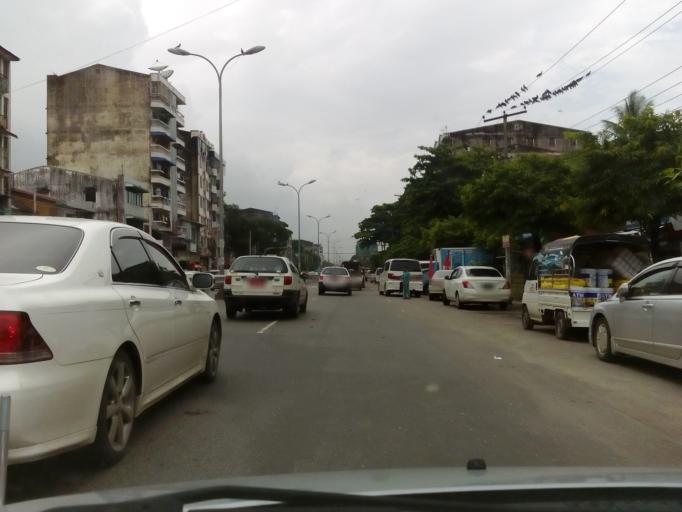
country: MM
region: Yangon
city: Yangon
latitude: 16.8134
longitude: 96.1700
